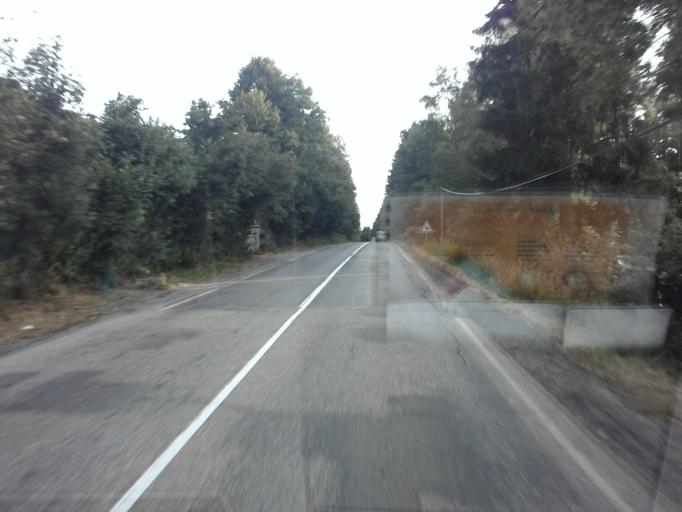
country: FR
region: Rhone-Alpes
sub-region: Departement de l'Isere
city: Pierre-Chatel
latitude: 44.9840
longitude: 5.7723
